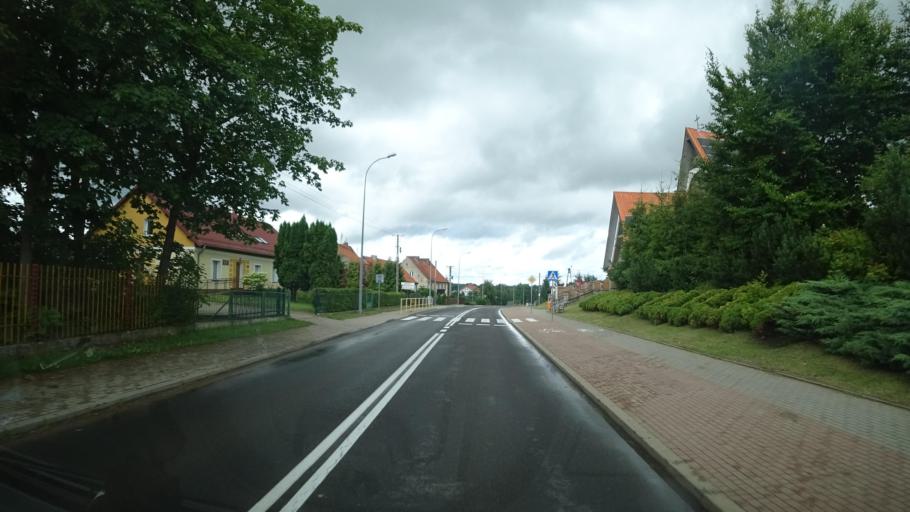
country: PL
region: Warmian-Masurian Voivodeship
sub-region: Powiat olecki
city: Kowale Oleckie
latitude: 54.1662
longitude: 22.4147
